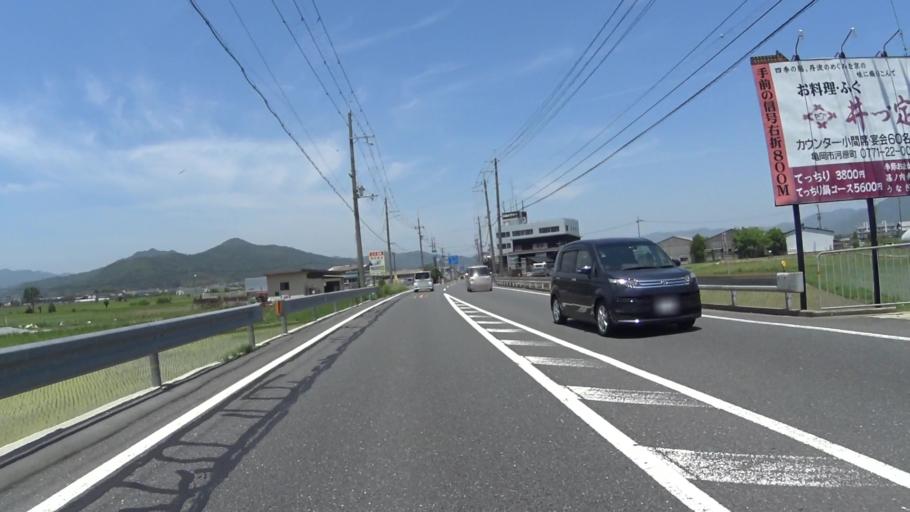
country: JP
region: Kyoto
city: Kameoka
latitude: 35.0184
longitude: 135.5626
